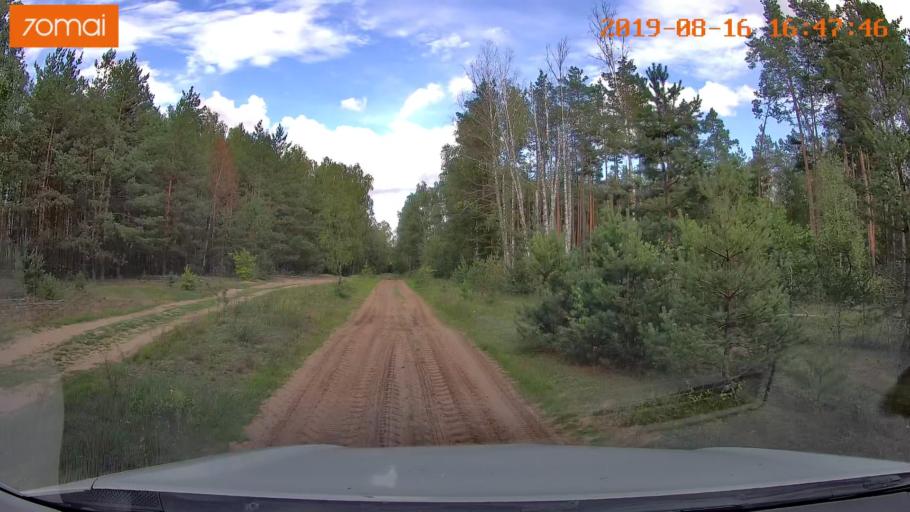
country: BY
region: Mogilev
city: Asipovichy
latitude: 53.2500
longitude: 28.7912
